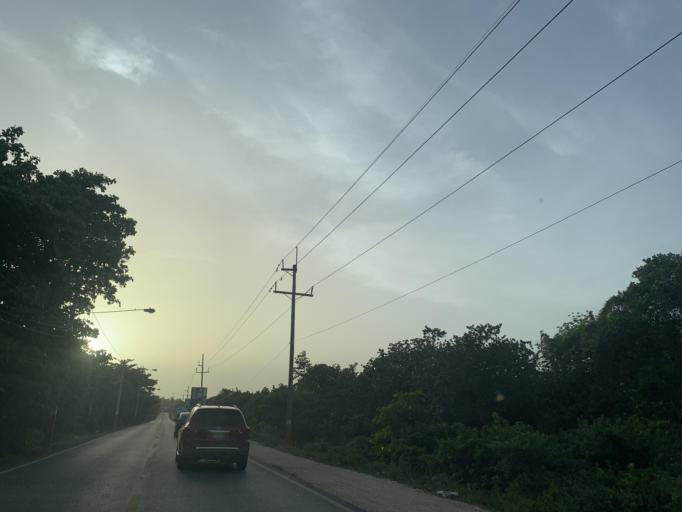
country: DO
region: Puerto Plata
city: Cabarete
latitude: 19.7702
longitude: -70.4364
